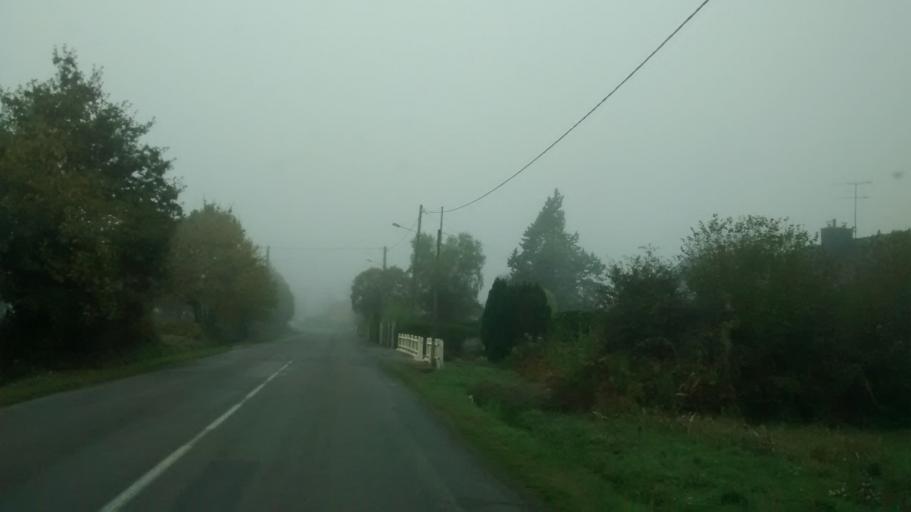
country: FR
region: Brittany
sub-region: Departement d'Ille-et-Vilaine
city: Liffre
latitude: 48.2064
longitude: -1.4983
